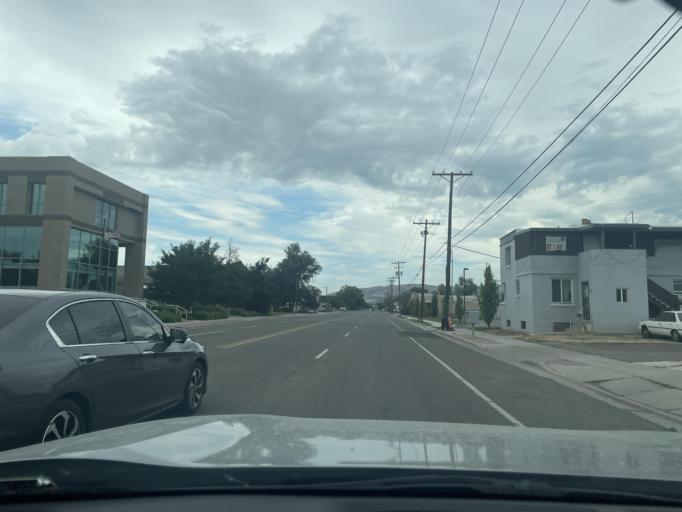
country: US
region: Utah
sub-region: Salt Lake County
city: Centerfield
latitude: 40.7027
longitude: -111.8911
